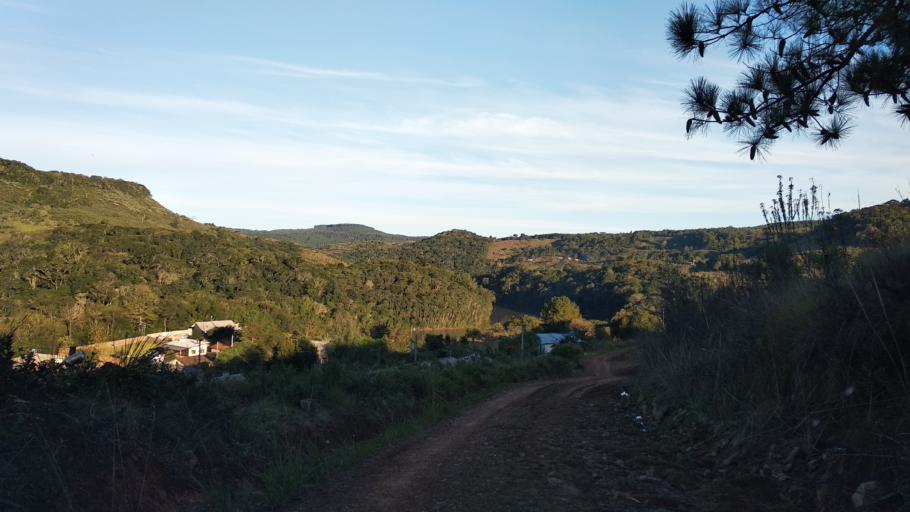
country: BR
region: Santa Catarina
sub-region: Celso Ramos
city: Celso Ramos
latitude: -27.5627
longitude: -51.2361
